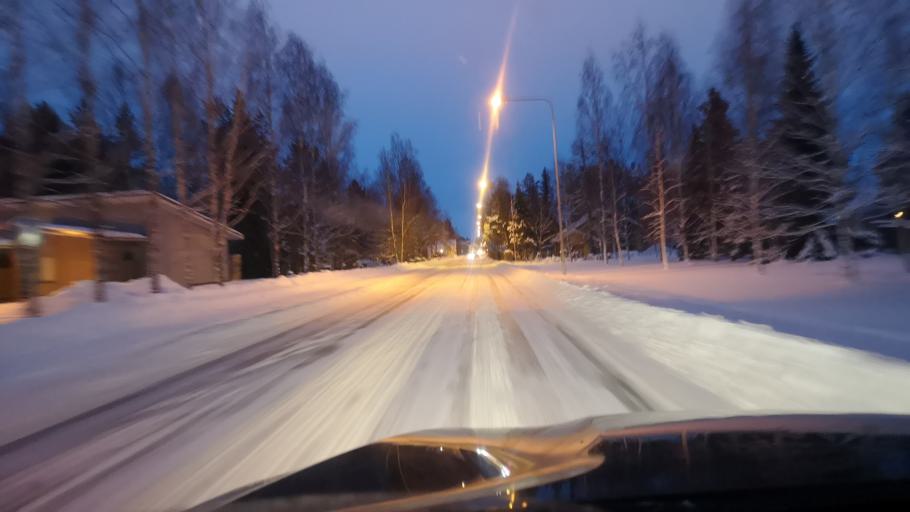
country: FI
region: Varsinais-Suomi
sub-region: Loimaa
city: Loimaa
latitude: 60.8563
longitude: 23.0651
